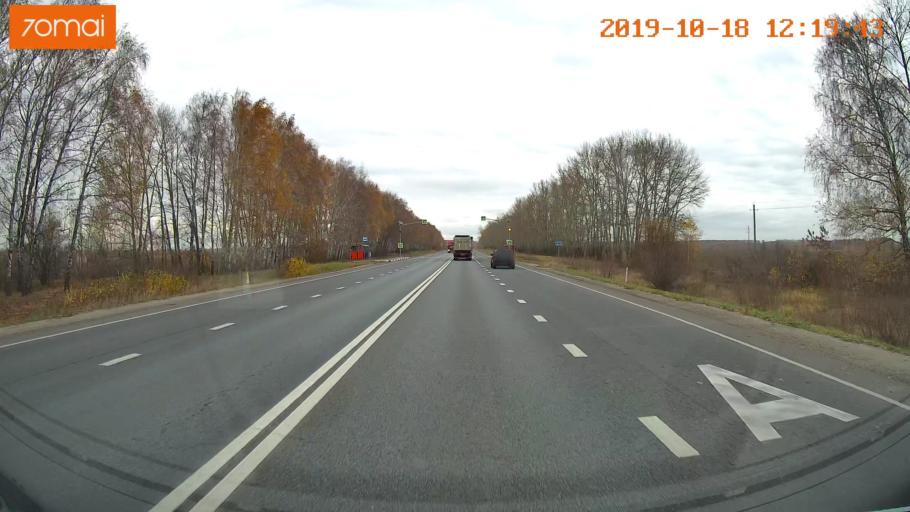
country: RU
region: Rjazan
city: Zakharovo
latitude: 54.4868
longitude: 39.4716
